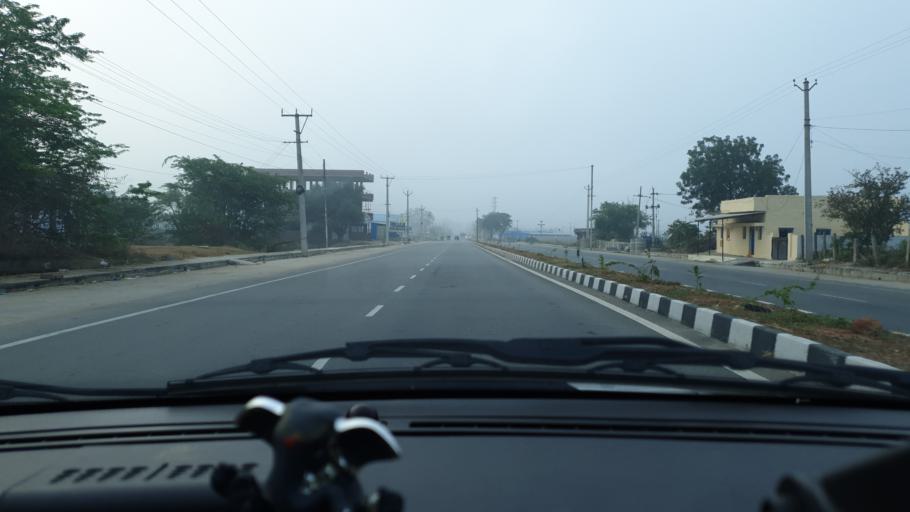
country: IN
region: Telangana
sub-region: Mahbubnagar
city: Farrukhnagar
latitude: 16.8796
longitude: 78.5292
